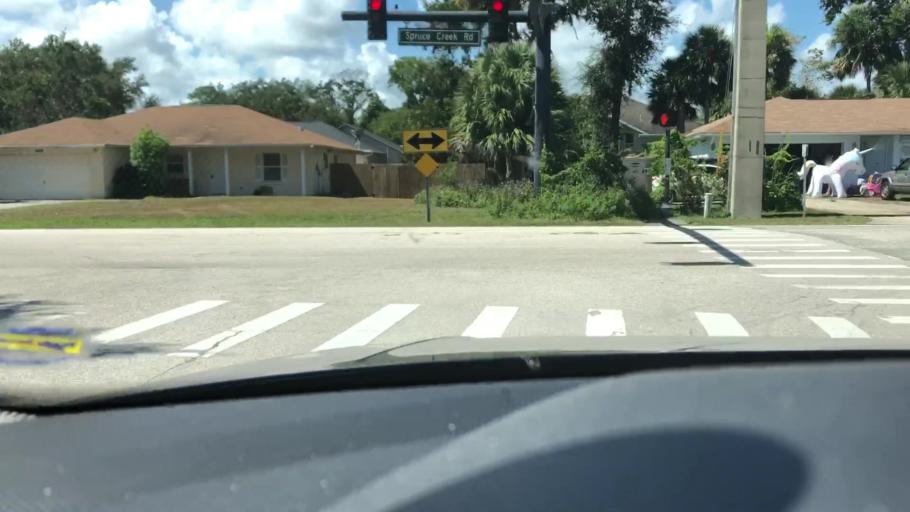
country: US
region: Florida
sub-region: Volusia County
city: Port Orange
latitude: 29.1242
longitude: -80.9929
